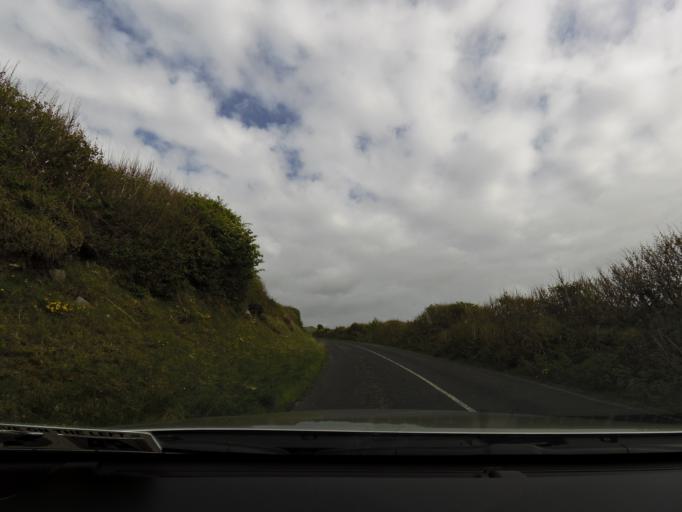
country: IE
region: Connaught
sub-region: County Galway
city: Bearna
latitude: 53.0554
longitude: -9.3517
